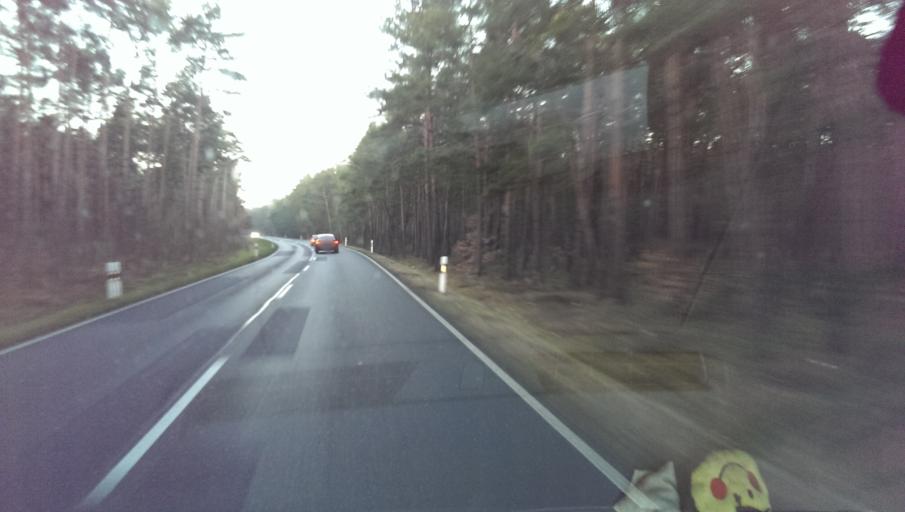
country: DE
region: Saxony-Anhalt
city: Holzdorf
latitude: 51.7800
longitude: 13.1950
